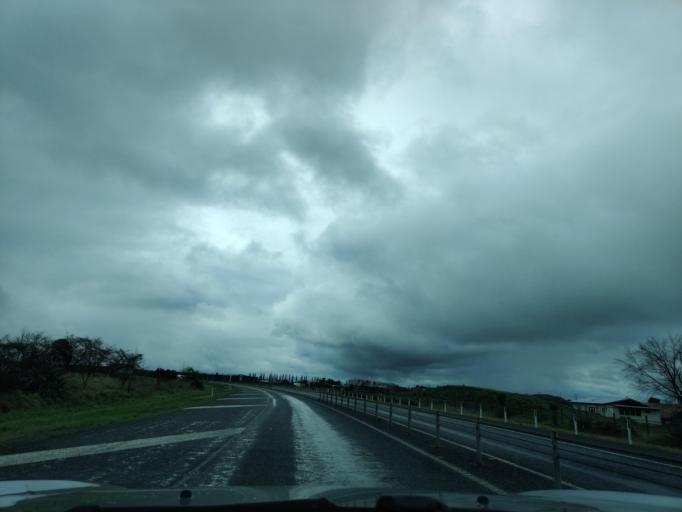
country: NZ
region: Hawke's Bay
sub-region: Hastings District
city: Hastings
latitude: -39.6546
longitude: 176.7953
